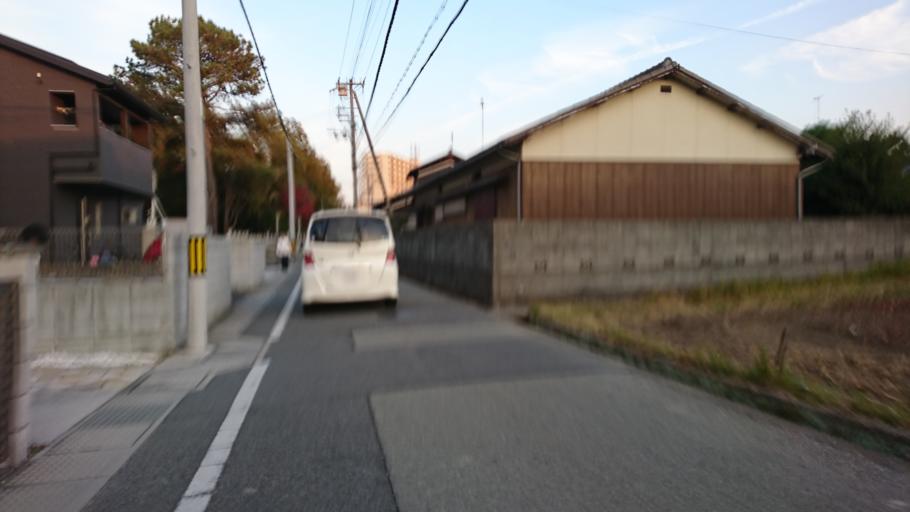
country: JP
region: Hyogo
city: Kakogawacho-honmachi
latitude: 34.7520
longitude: 134.8583
